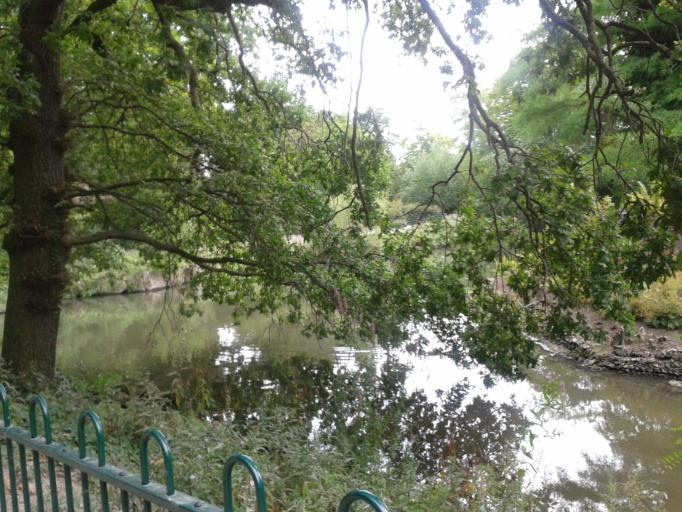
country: GB
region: England
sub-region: Greater London
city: Thornton Heath
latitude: 51.4177
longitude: -0.0675
